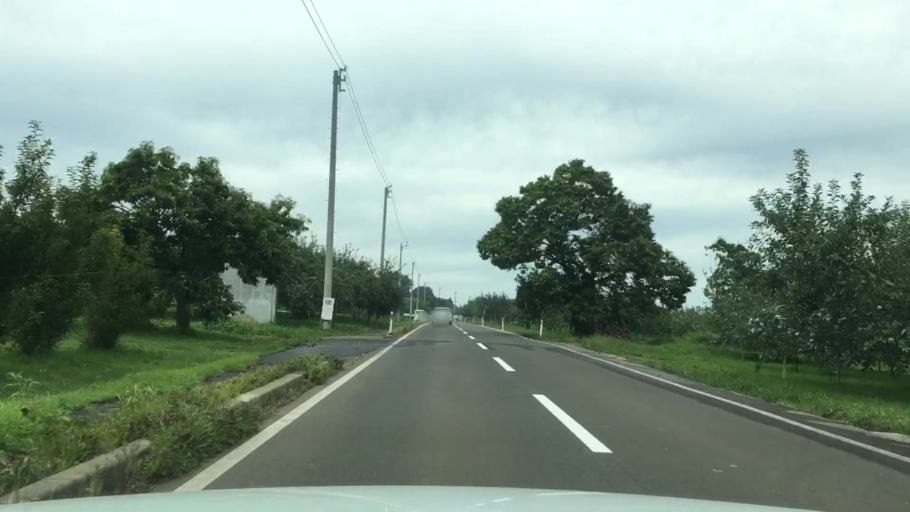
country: JP
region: Aomori
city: Hirosaki
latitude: 40.6699
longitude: 140.3884
